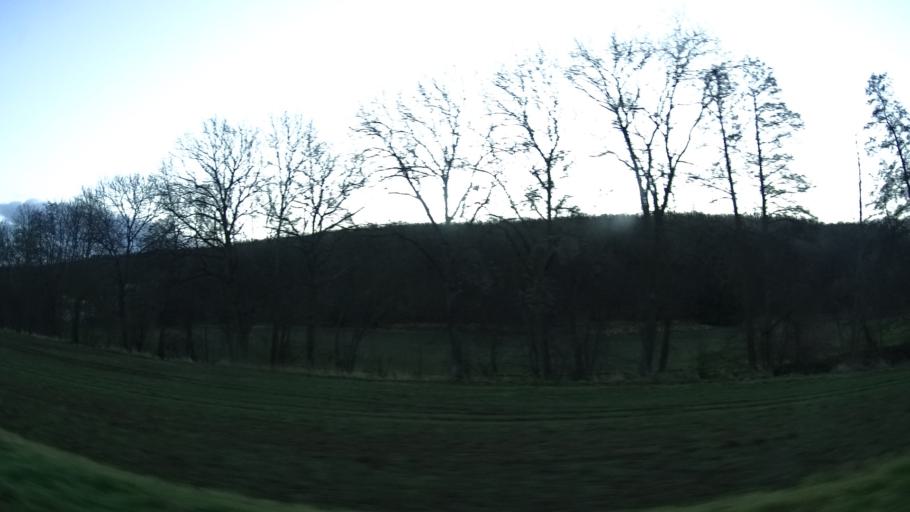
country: DE
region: Rheinland-Pfalz
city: Wendelsheim
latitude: 49.7580
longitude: 7.9913
